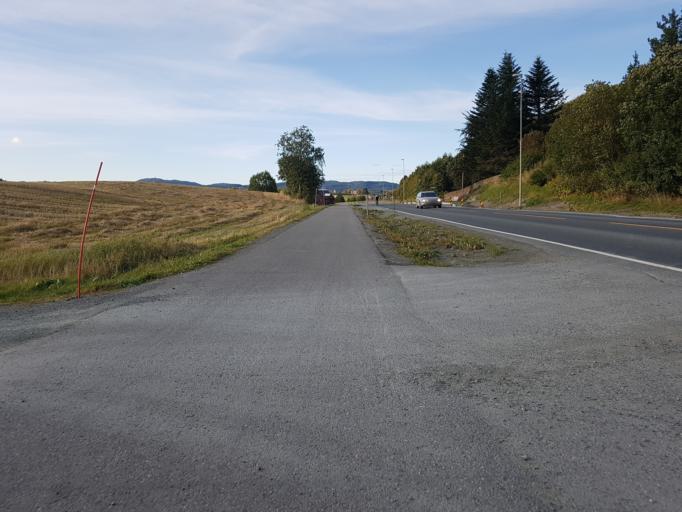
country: NO
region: Sor-Trondelag
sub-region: Trondheim
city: Trondheim
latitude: 63.3719
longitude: 10.4337
